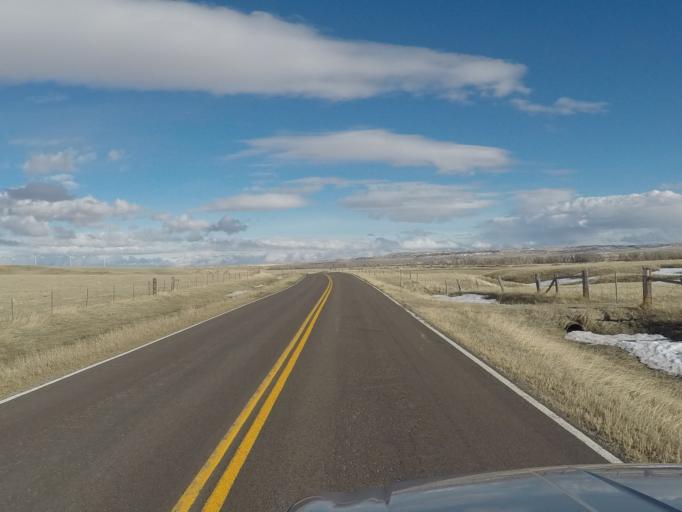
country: US
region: Montana
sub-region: Wheatland County
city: Harlowton
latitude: 46.4434
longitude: -110.1389
